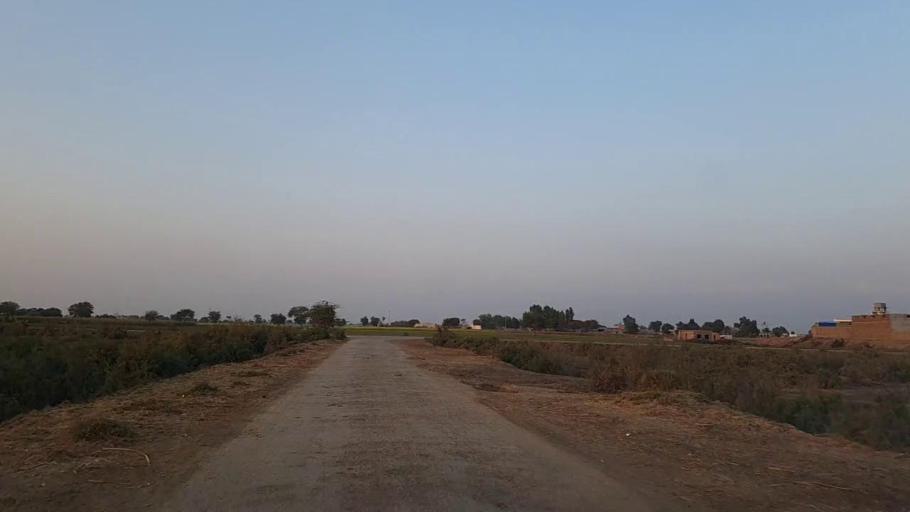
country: PK
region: Sindh
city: Jam Sahib
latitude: 26.3111
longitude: 68.5836
